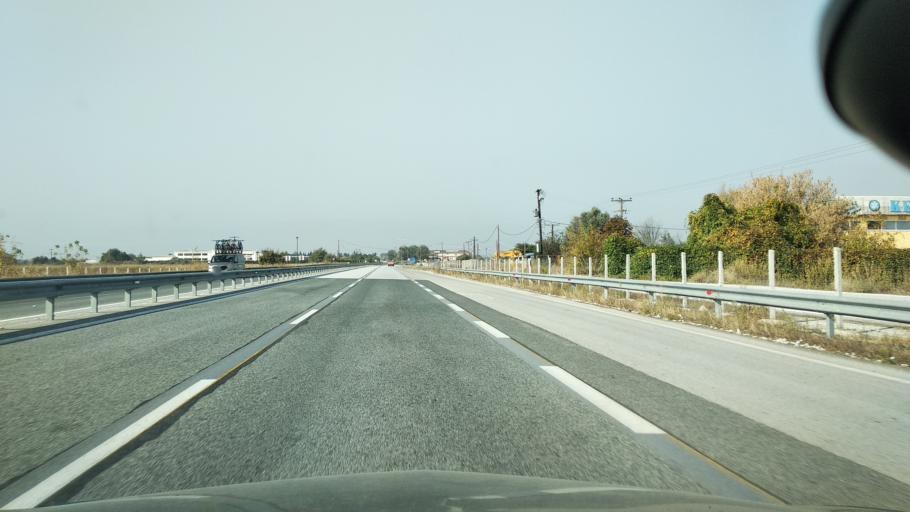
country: GR
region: Thessaly
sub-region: Trikala
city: Megalochori
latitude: 39.5623
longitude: 21.8637
